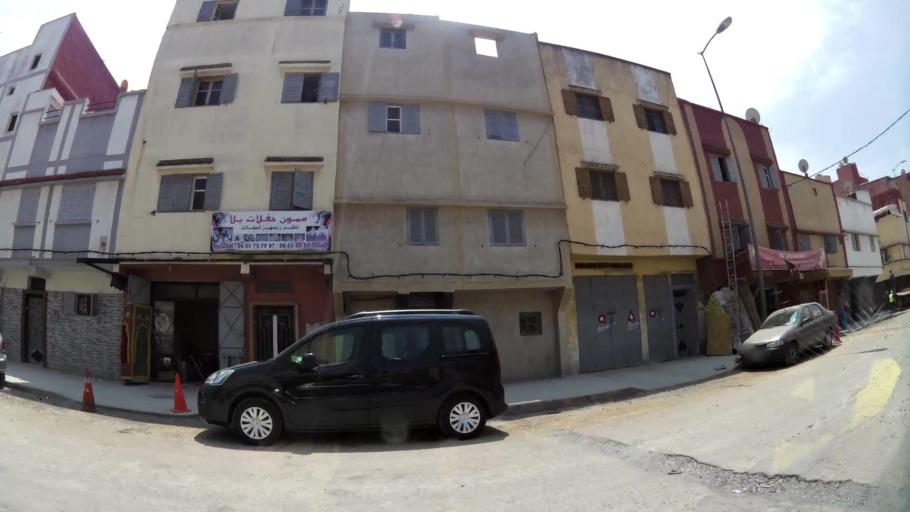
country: MA
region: Rabat-Sale-Zemmour-Zaer
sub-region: Rabat
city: Rabat
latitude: 33.9870
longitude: -6.8813
